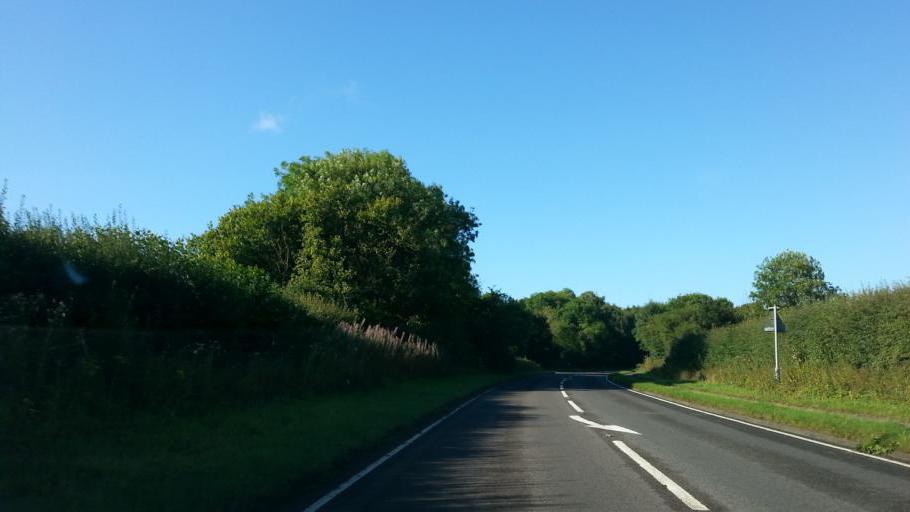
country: GB
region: England
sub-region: Lincolnshire
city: Stamford
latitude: 52.6414
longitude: -0.4852
